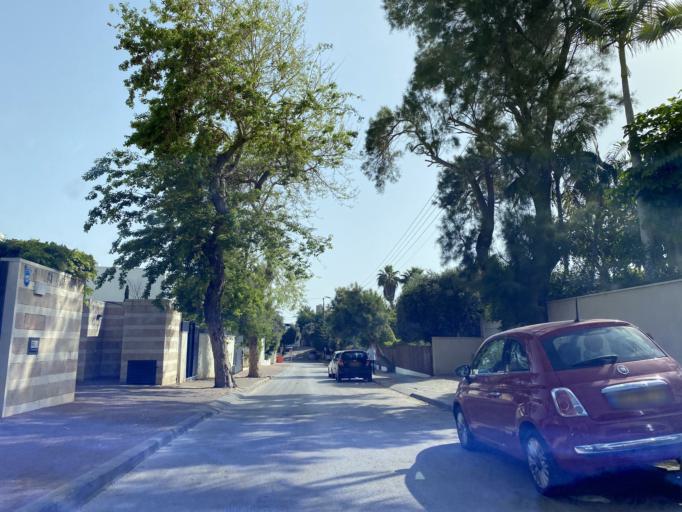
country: IL
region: Tel Aviv
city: Herzliya Pituah
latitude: 32.1753
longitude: 34.8066
